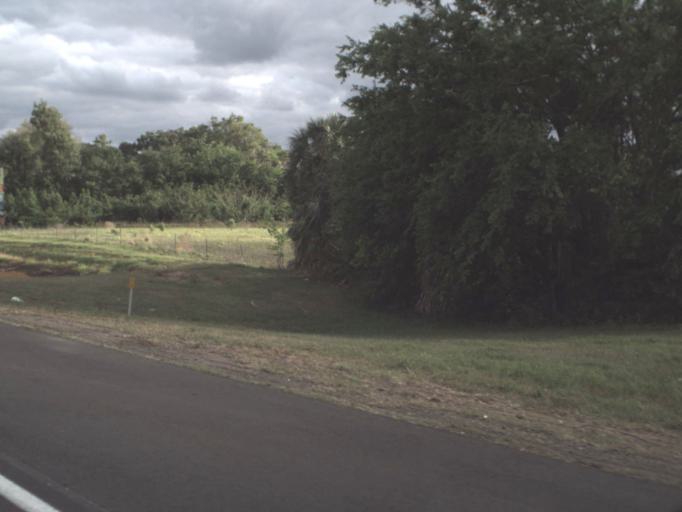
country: US
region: Florida
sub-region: Marion County
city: Ocala
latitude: 29.2976
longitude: -82.2045
